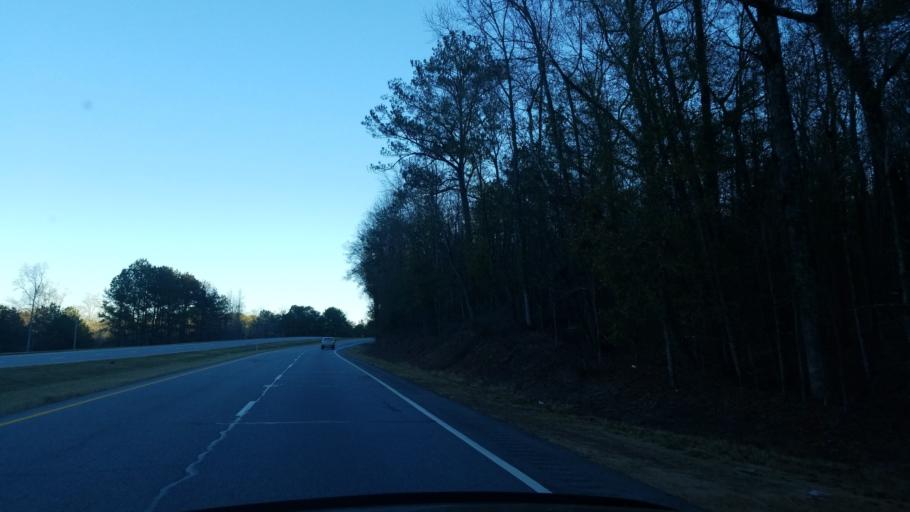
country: US
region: Georgia
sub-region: Chattahoochee County
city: Cusseta
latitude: 32.2632
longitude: -84.7361
